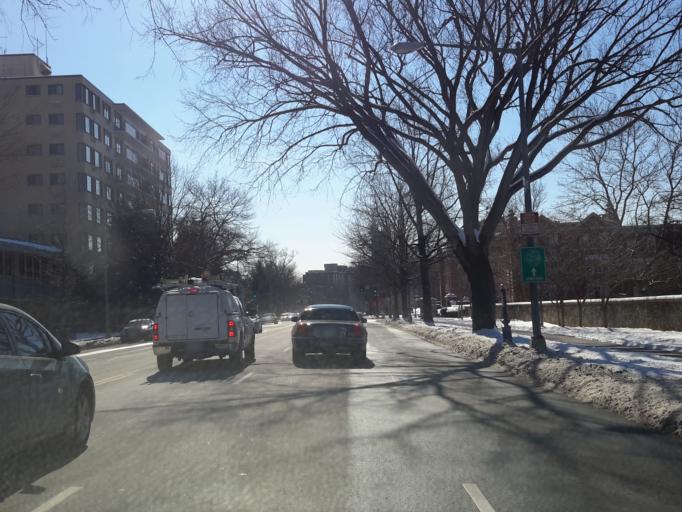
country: US
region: Maryland
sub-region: Montgomery County
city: Friendship Village
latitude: 38.9384
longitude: -77.0744
